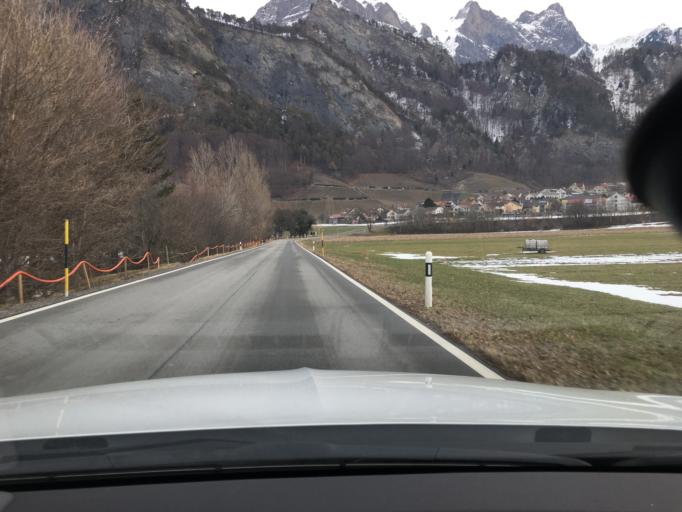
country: CH
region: Saint Gallen
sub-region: Wahlkreis Sarganserland
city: Bad Ragaz
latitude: 47.0255
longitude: 9.5047
